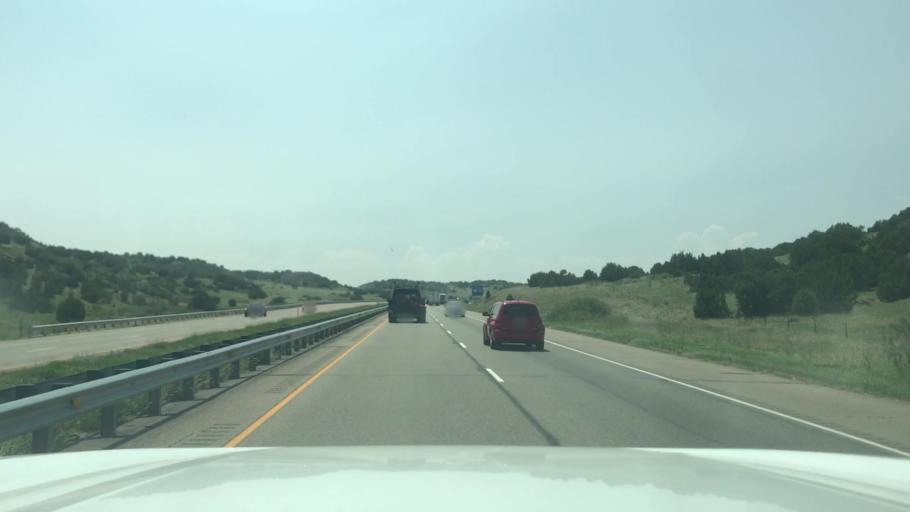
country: US
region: Colorado
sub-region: Pueblo County
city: Colorado City
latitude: 37.9787
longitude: -104.7781
